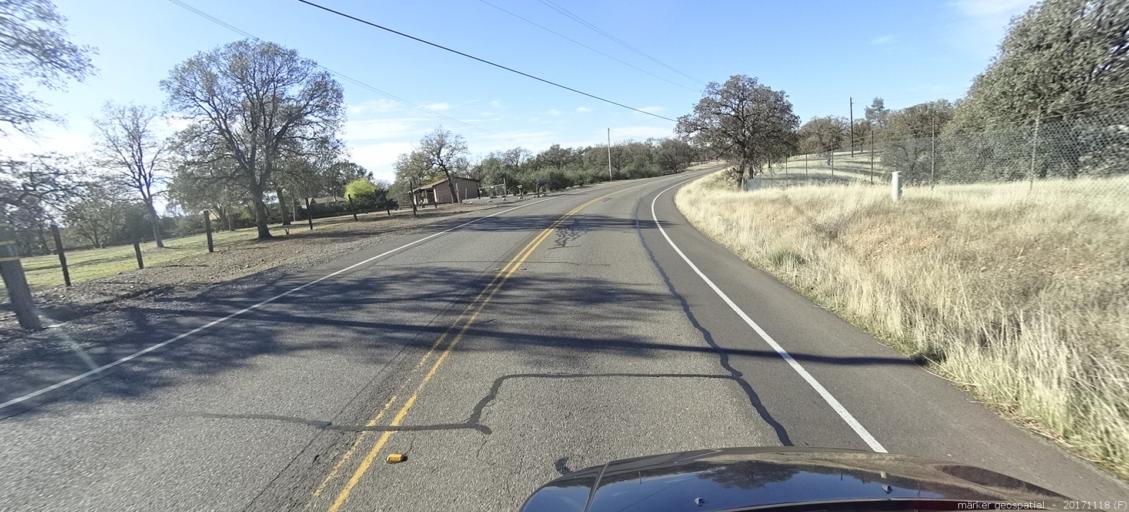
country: US
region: California
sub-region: Shasta County
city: Anderson
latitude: 40.4402
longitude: -122.3323
